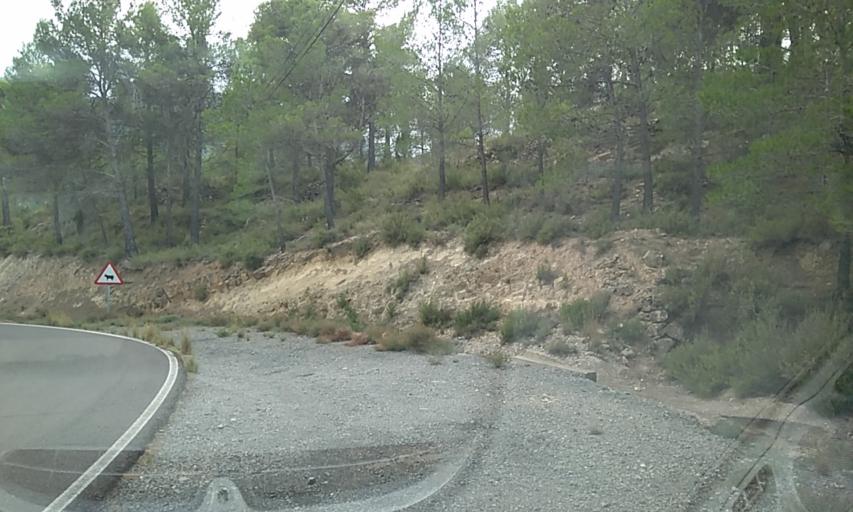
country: ES
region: Valencia
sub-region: Provincia de Castello
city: Puebla de Arenoso
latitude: 40.0968
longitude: -0.5726
